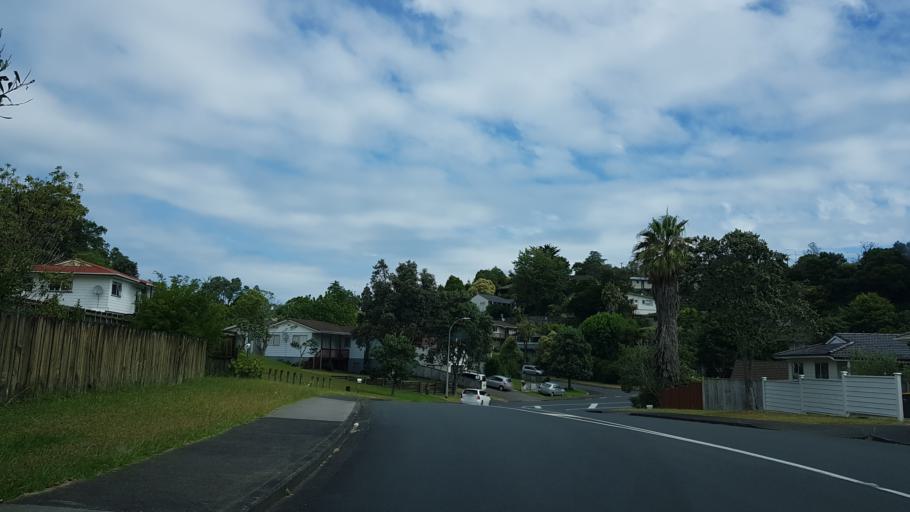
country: NZ
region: Auckland
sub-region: Auckland
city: North Shore
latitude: -36.7718
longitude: 174.7159
